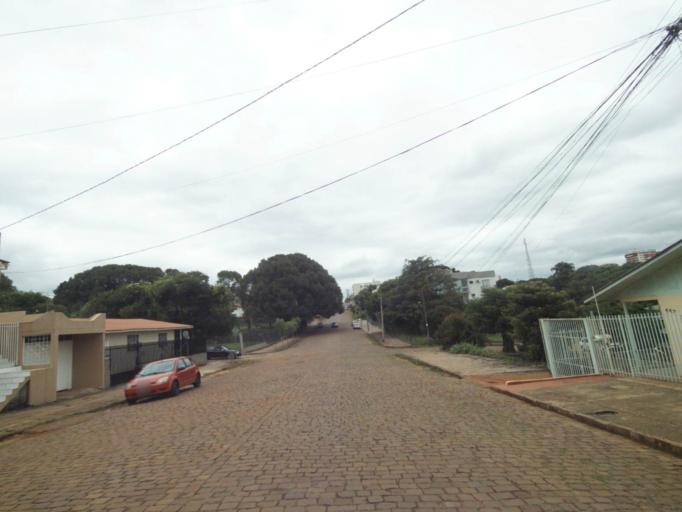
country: BR
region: Rio Grande do Sul
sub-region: Lagoa Vermelha
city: Lagoa Vermelha
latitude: -28.2058
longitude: -51.5244
